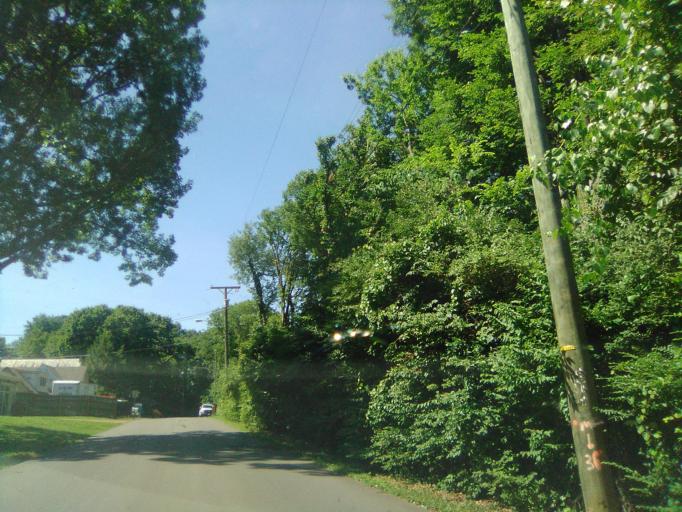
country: US
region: Tennessee
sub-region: Davidson County
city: Belle Meade
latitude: 36.1261
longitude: -86.8384
